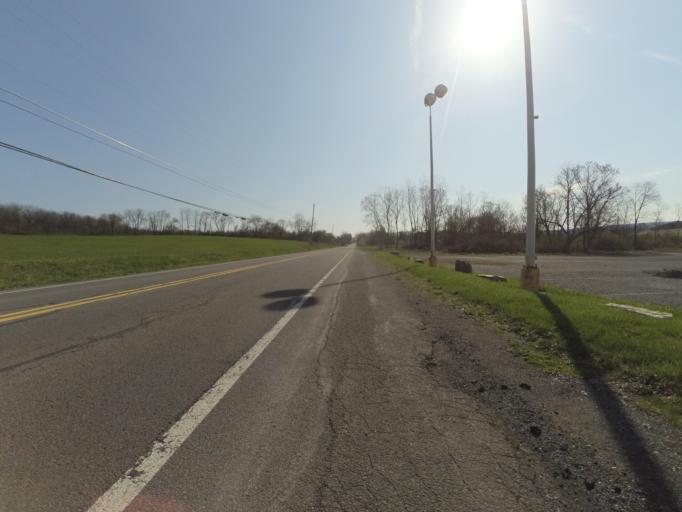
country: US
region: Pennsylvania
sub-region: Centre County
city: Bellefonte
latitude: 40.9158
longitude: -77.7318
